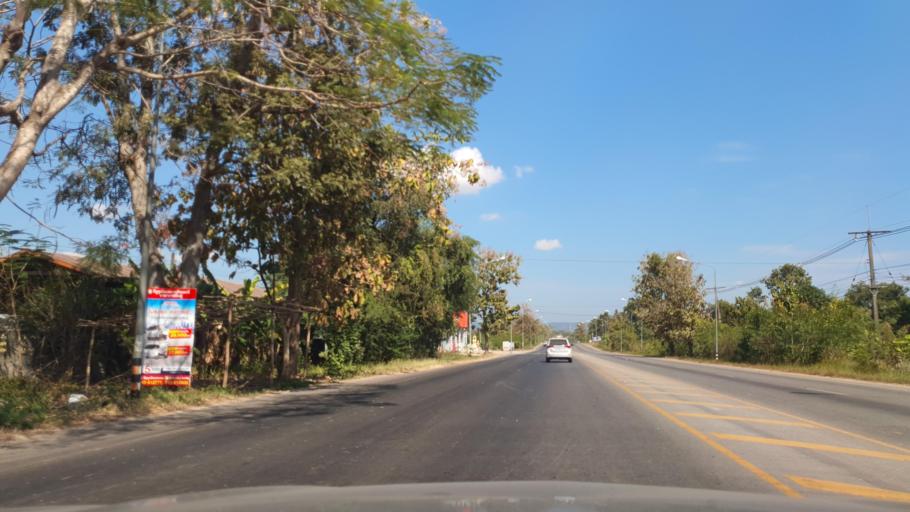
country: TH
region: Kalasin
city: Somdet
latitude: 16.7326
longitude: 103.7650
